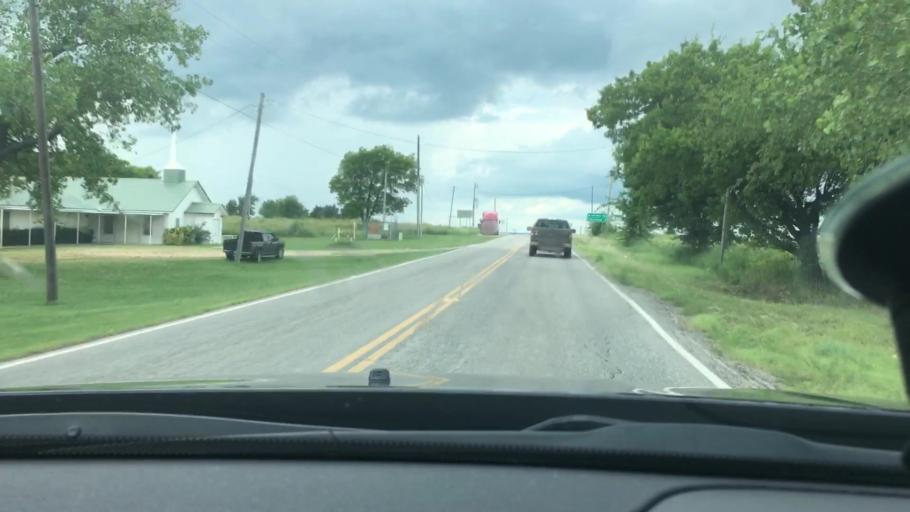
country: US
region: Oklahoma
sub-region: Bryan County
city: Durant
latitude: 34.1433
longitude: -96.5004
